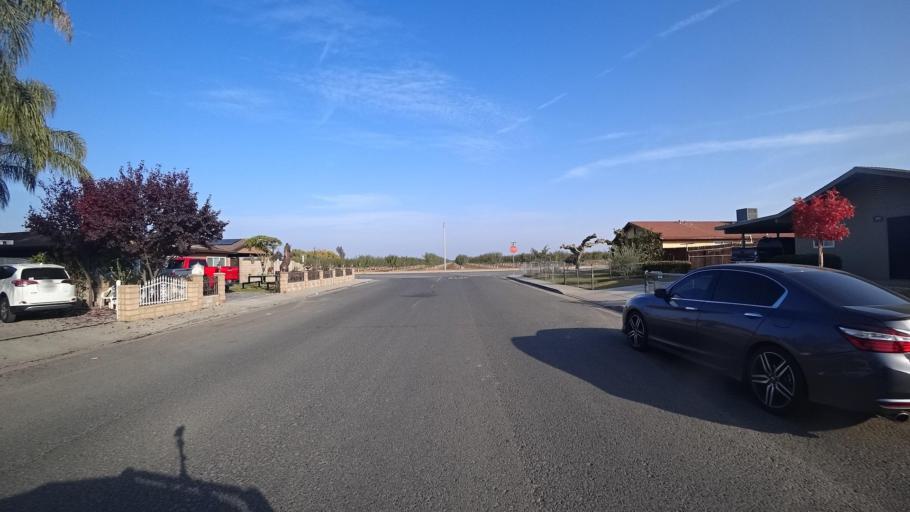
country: US
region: California
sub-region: Kern County
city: McFarland
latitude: 35.6811
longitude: -119.2196
